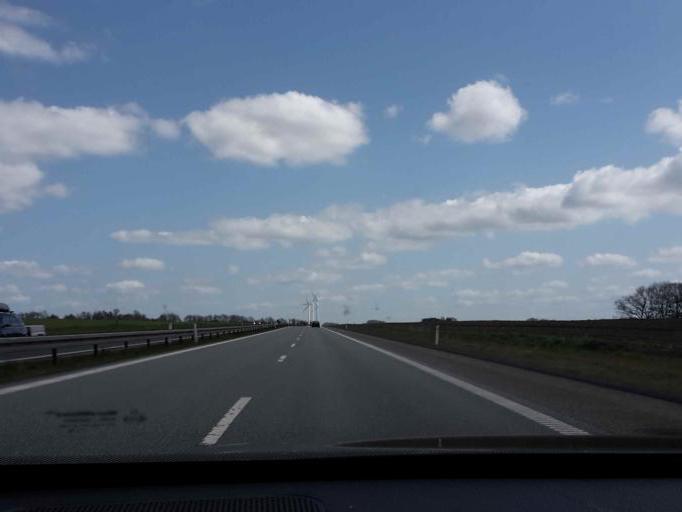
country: DK
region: South Denmark
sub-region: Vejen Kommune
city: Brorup
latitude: 55.5102
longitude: 8.9777
